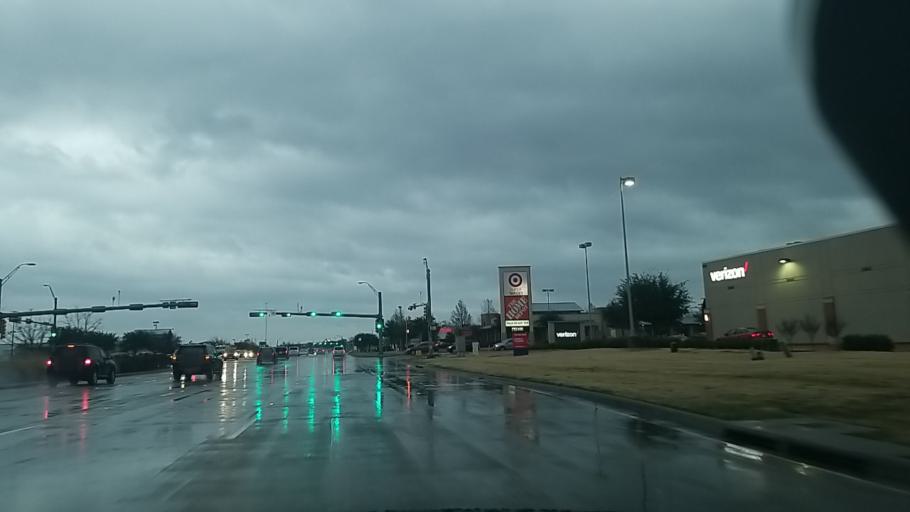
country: US
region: Texas
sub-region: Denton County
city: Denton
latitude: 33.1910
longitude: -97.1001
